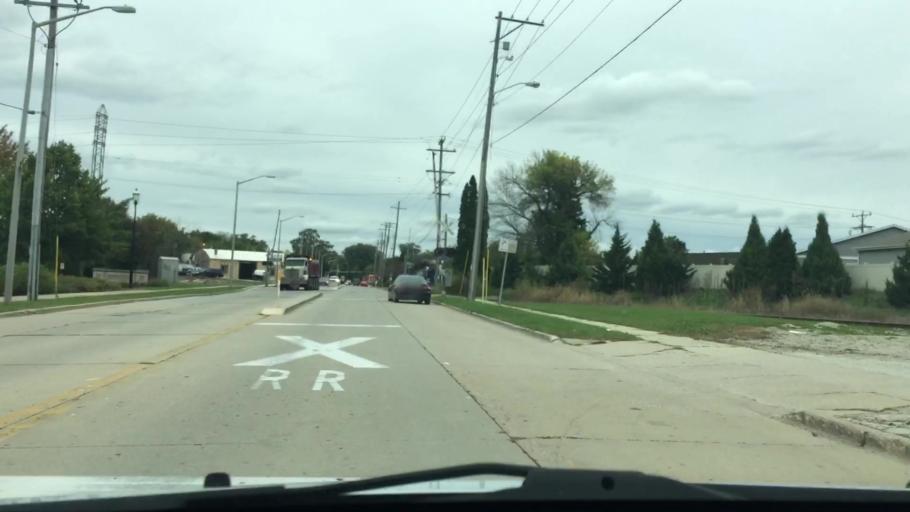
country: US
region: Wisconsin
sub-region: Waukesha County
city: Waukesha
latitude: 43.0188
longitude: -88.2211
